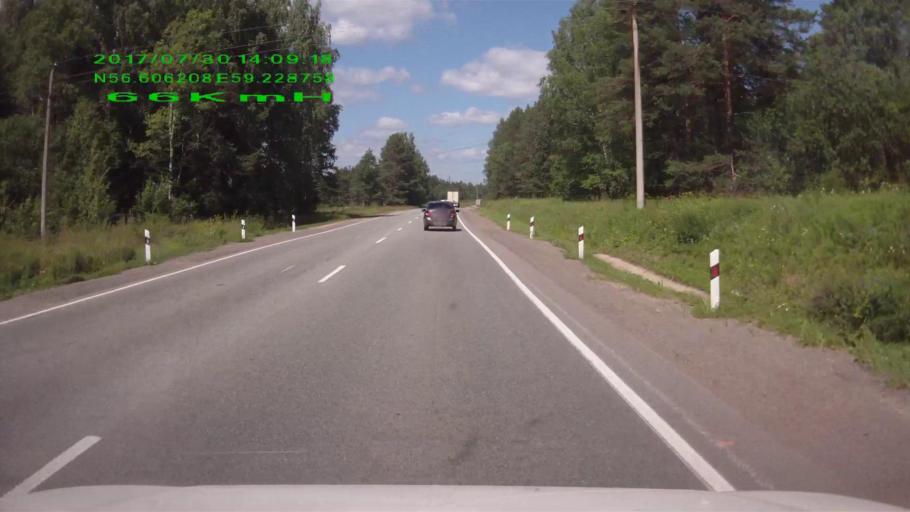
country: RU
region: Sverdlovsk
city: Nizhniye Sergi
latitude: 56.6066
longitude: 59.2287
